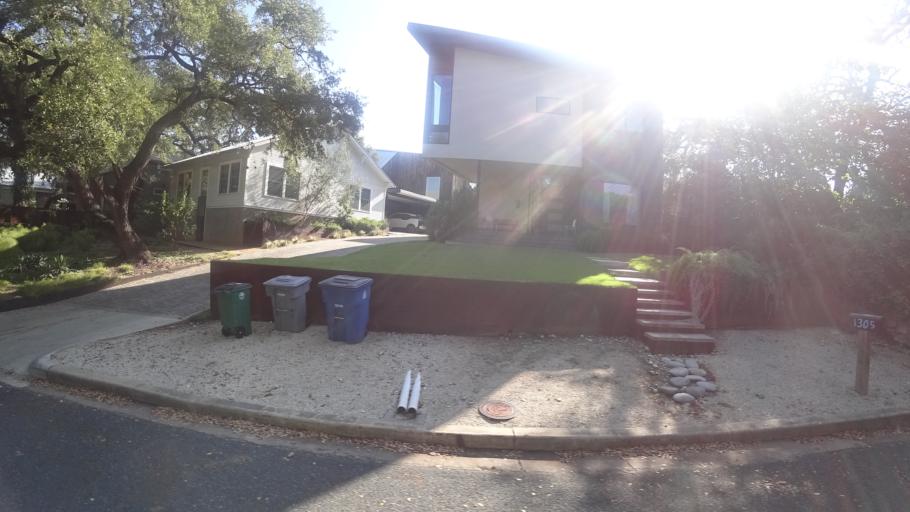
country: US
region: Texas
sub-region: Travis County
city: Austin
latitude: 30.2494
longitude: -97.7462
